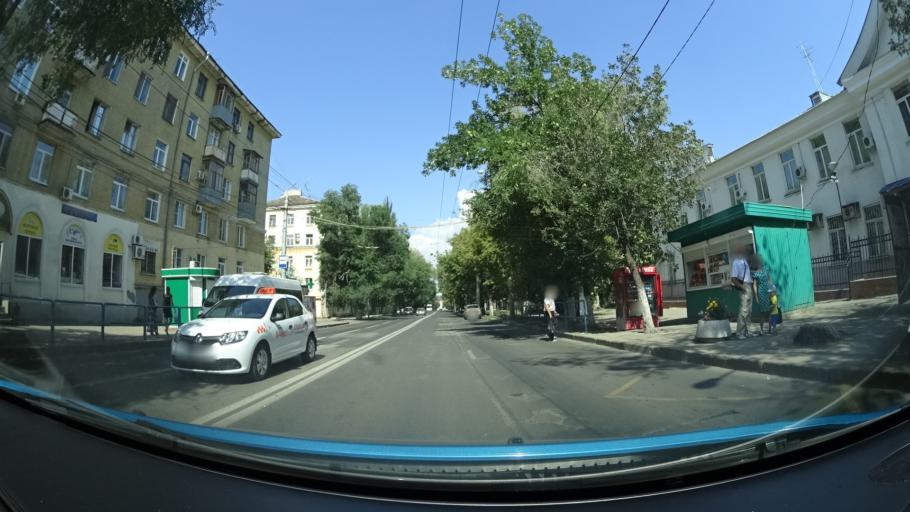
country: RU
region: Samara
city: Samara
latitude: 53.2113
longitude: 50.1556
